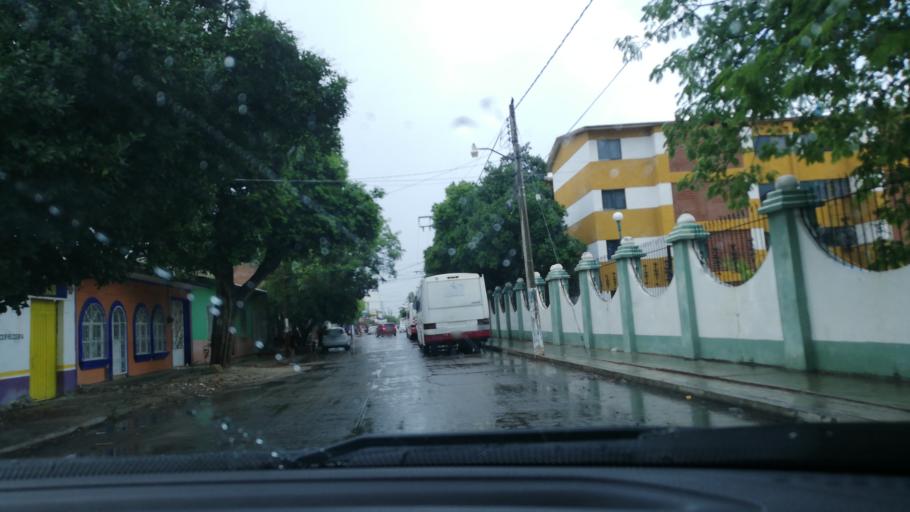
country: MX
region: Oaxaca
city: San Jeronimo Ixtepec
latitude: 16.5554
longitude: -95.0979
